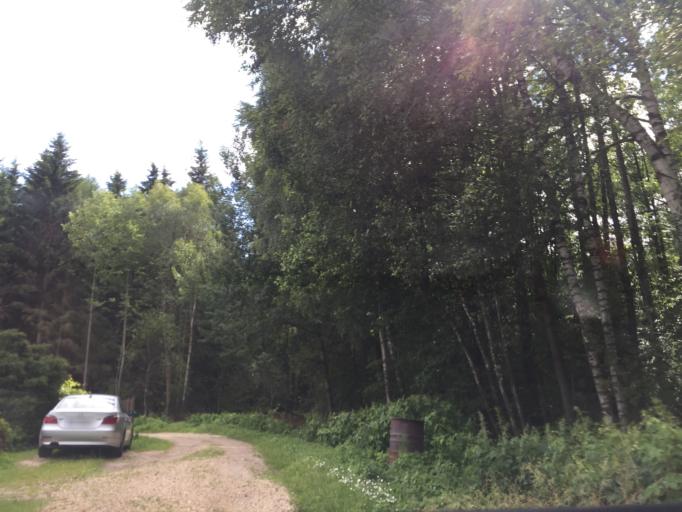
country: LV
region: Carnikava
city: Carnikava
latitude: 57.1175
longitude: 24.2230
